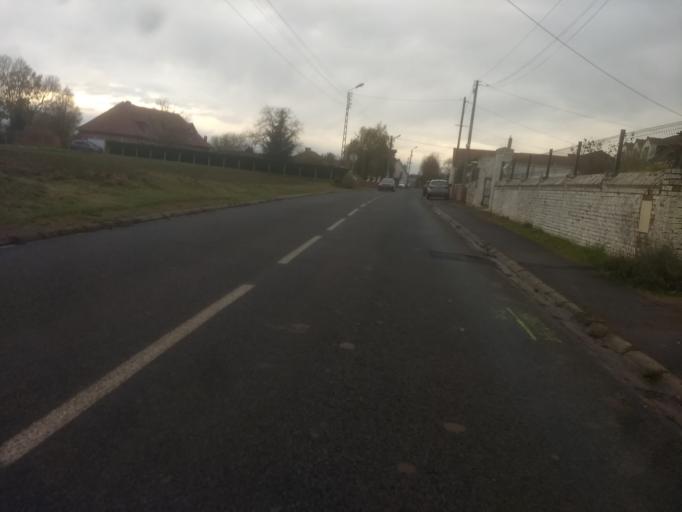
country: FR
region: Nord-Pas-de-Calais
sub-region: Departement du Pas-de-Calais
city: Riviere
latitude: 50.2367
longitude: 2.7034
